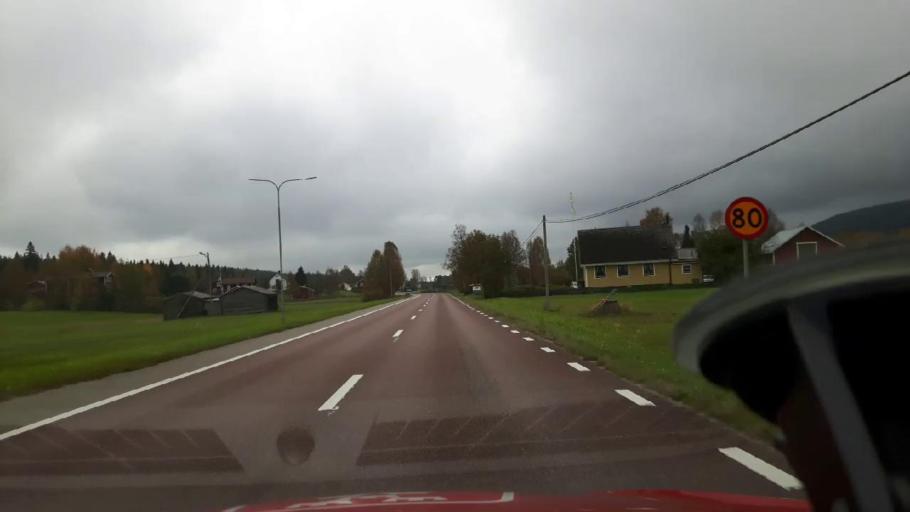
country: SE
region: Jaemtland
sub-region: Harjedalens Kommun
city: Sveg
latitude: 62.2848
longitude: 14.7987
